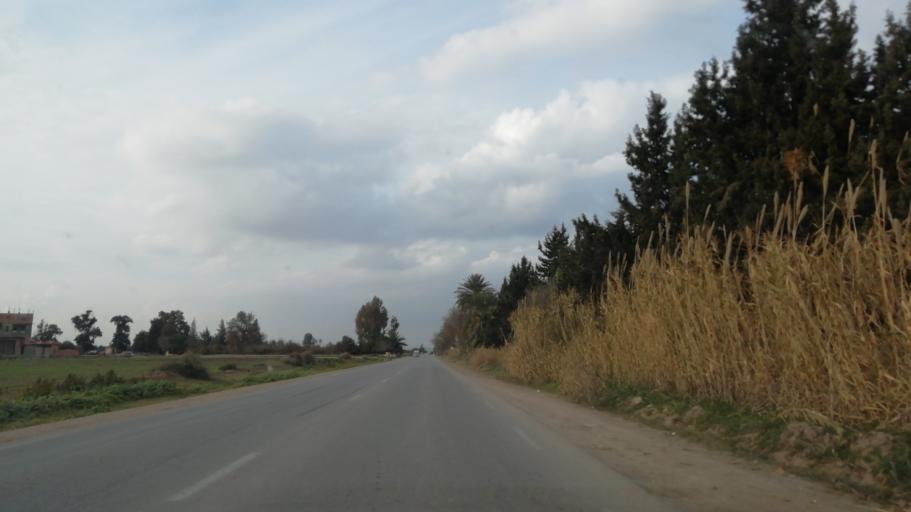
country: DZ
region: Mascara
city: Sig
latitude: 35.6807
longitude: -0.0104
